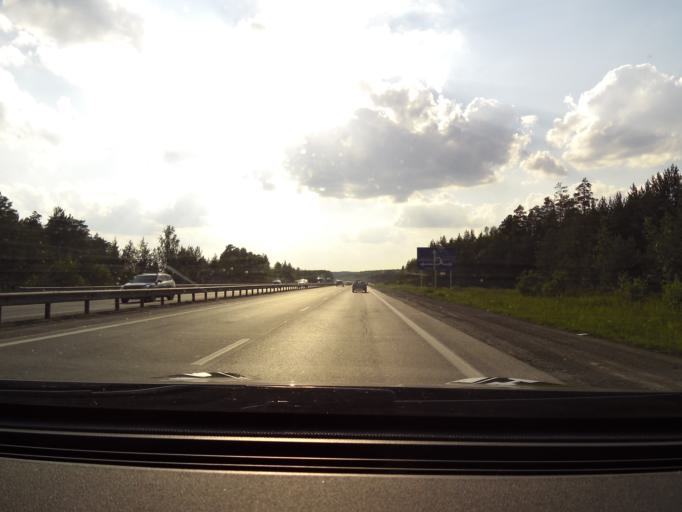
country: RU
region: Sverdlovsk
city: Severka
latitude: 56.8426
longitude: 60.2480
